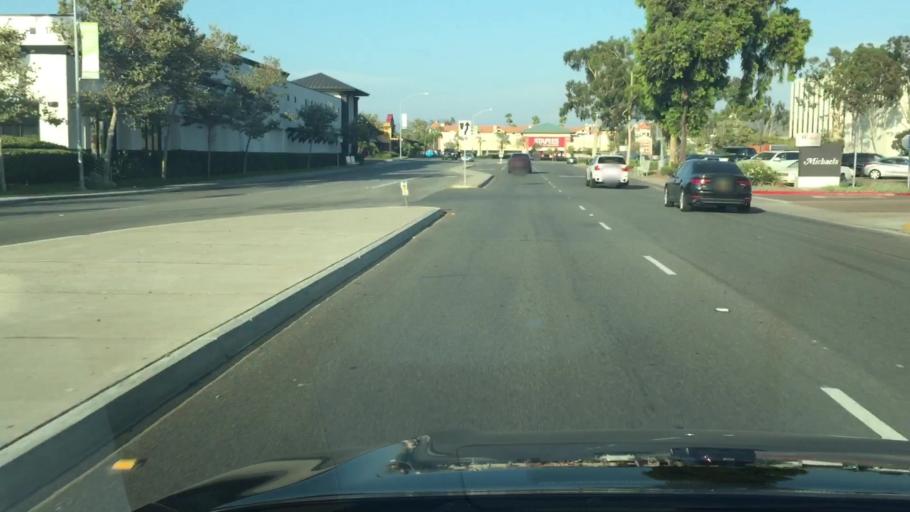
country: US
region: California
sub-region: San Diego County
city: San Diego
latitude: 32.7705
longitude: -117.1479
